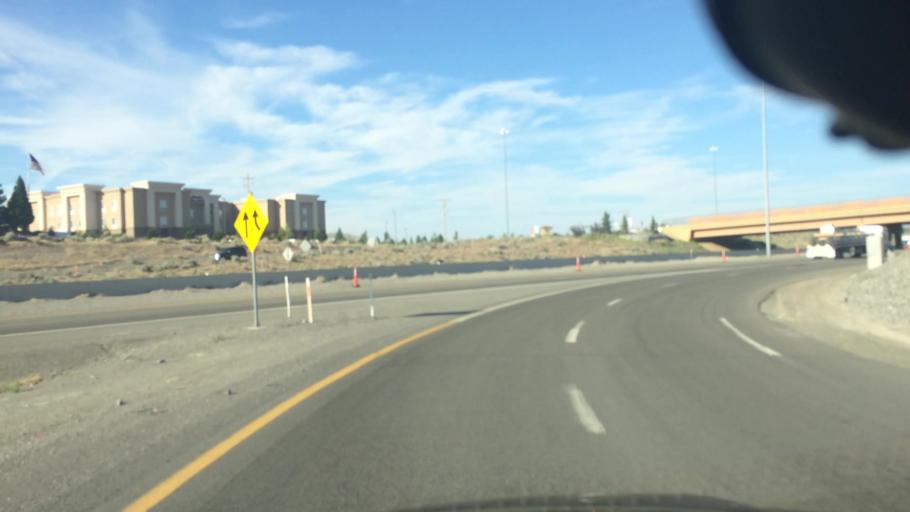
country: US
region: Nevada
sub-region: Washoe County
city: Mogul
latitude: 39.5153
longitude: -119.8890
